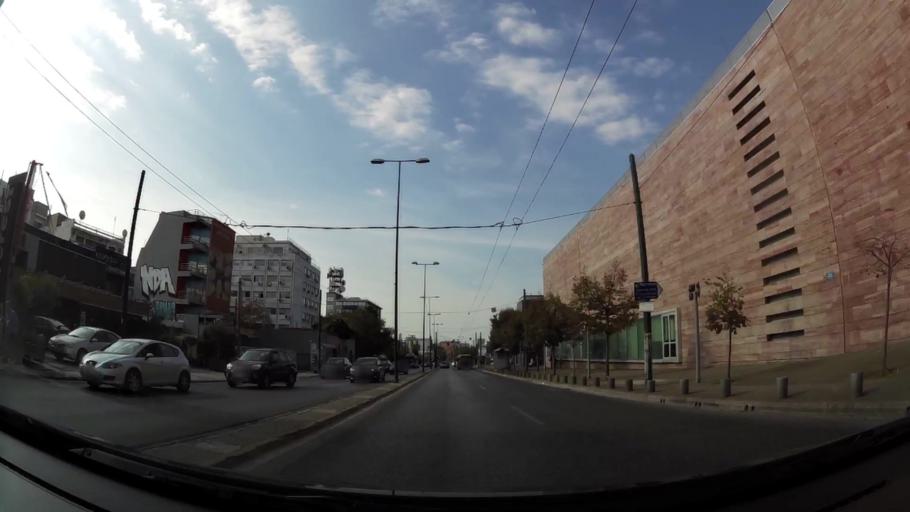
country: GR
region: Attica
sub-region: Nomarchia Athinas
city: Athens
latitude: 37.9744
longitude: 23.7087
